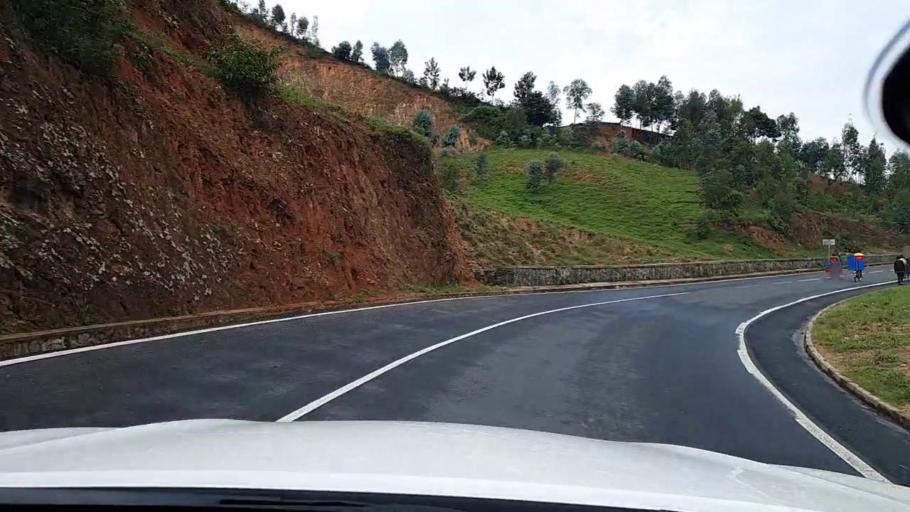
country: RW
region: Western Province
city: Kibuye
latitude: -2.1560
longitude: 29.2986
